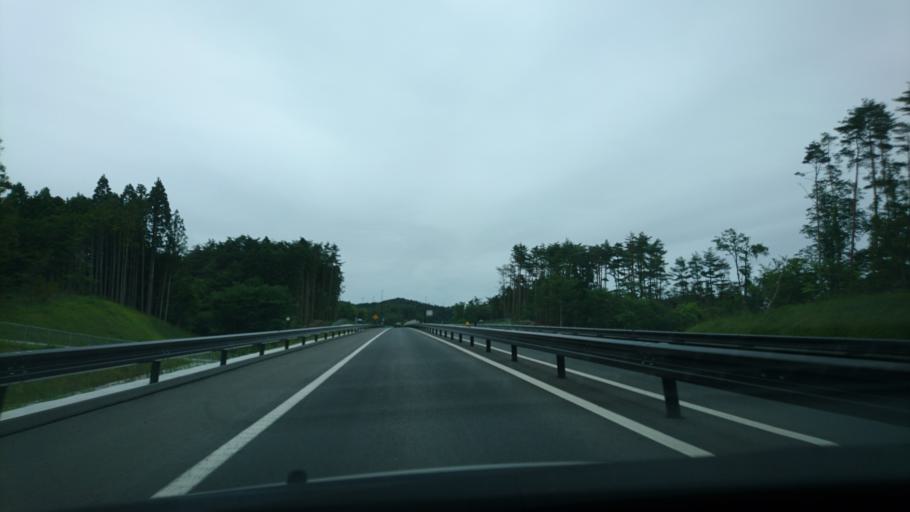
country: JP
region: Miyagi
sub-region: Oshika Gun
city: Onagawa Cho
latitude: 38.6932
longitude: 141.4631
